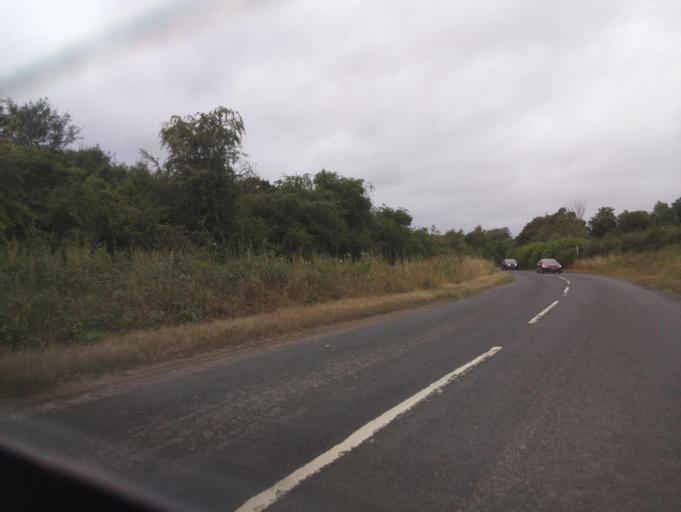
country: GB
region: England
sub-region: Derbyshire
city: Swadlincote
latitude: 52.7903
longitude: -1.5331
